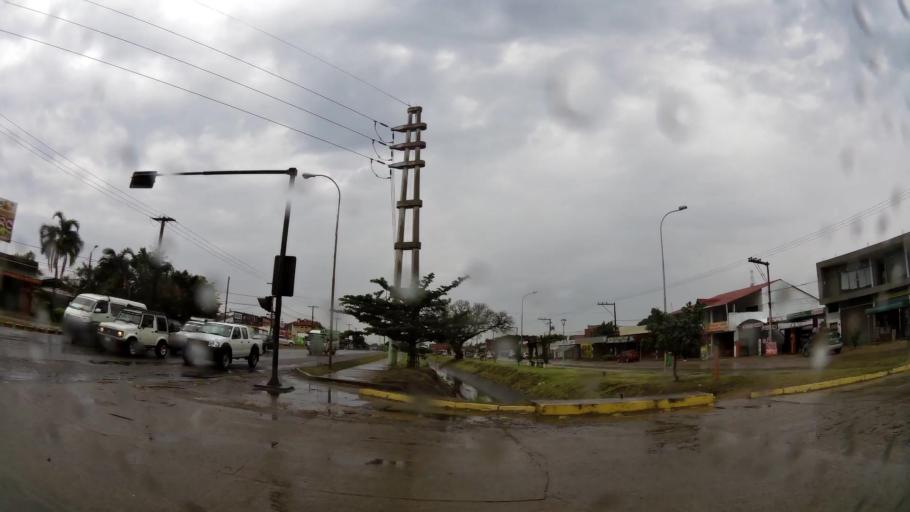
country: BO
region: Santa Cruz
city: Santa Cruz de la Sierra
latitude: -17.8057
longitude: -63.1540
